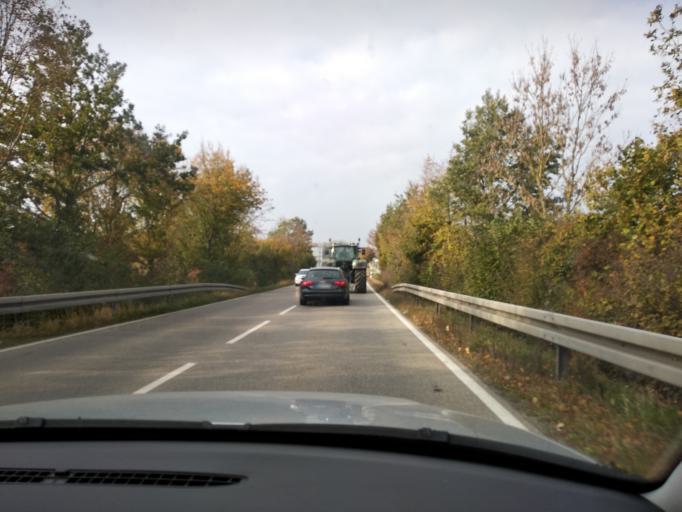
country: DE
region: Bavaria
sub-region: Upper Bavaria
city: Forstinning
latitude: 48.1722
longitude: 11.8886
